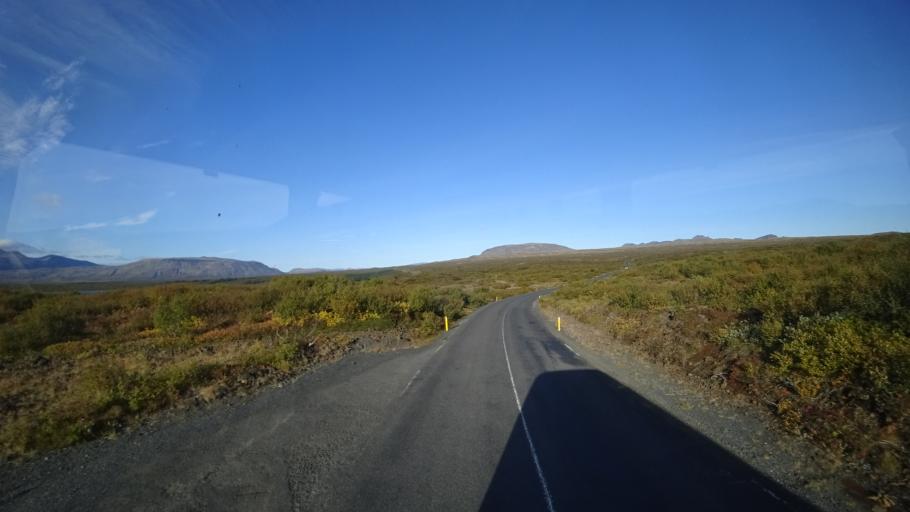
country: IS
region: South
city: Hveragerdi
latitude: 64.2299
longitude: -21.0504
